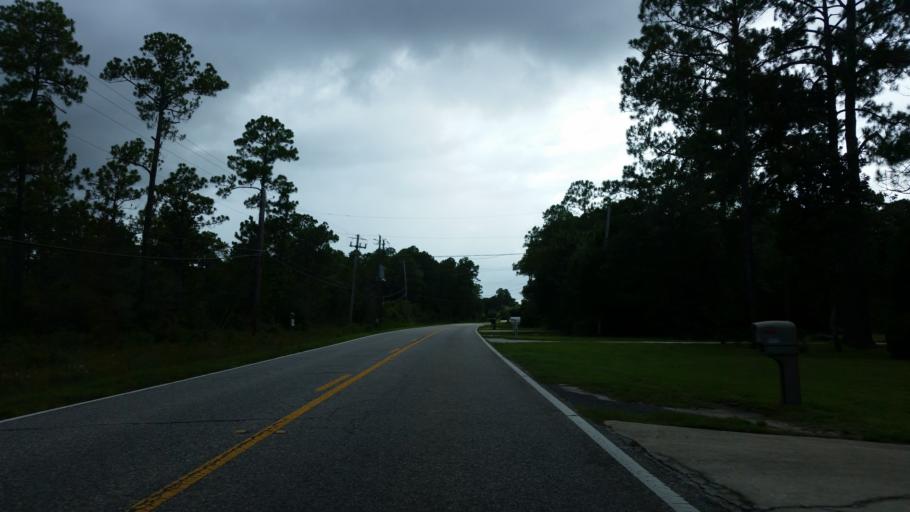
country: US
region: Florida
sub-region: Santa Rosa County
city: Holley
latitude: 30.4342
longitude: -86.9598
